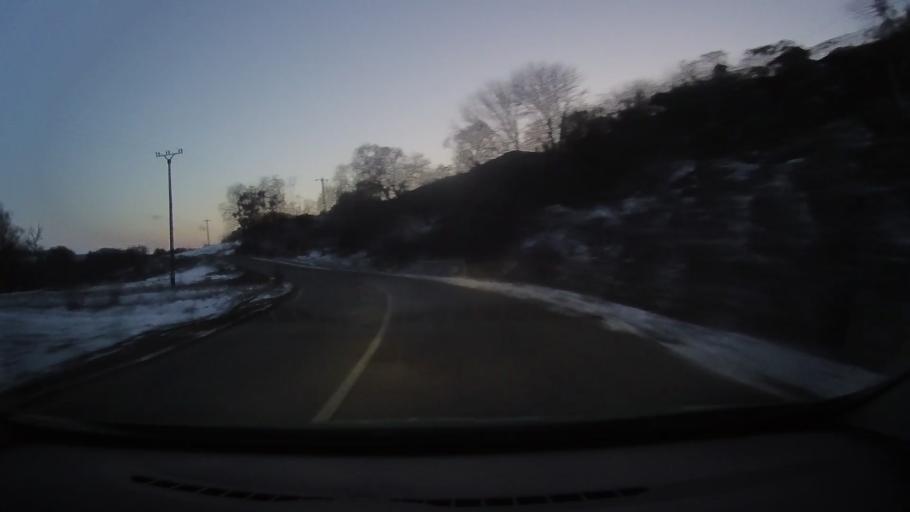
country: RO
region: Sibiu
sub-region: Comuna Alma
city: Alma
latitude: 46.1978
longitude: 24.4438
